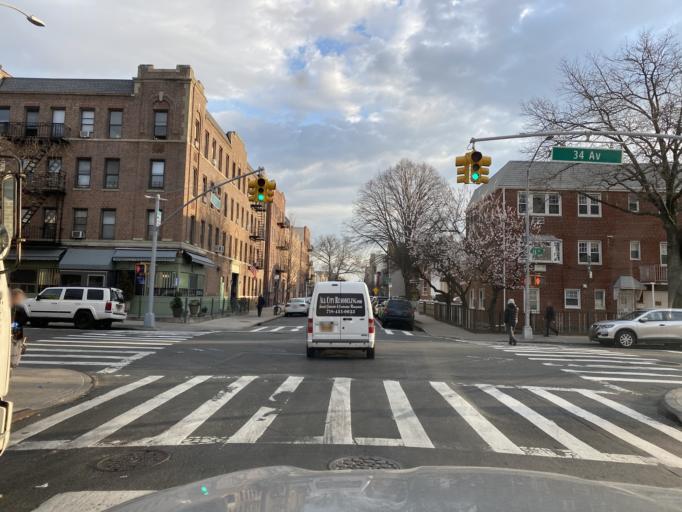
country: US
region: New York
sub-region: Queens County
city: Long Island City
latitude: 40.7580
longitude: -73.9241
